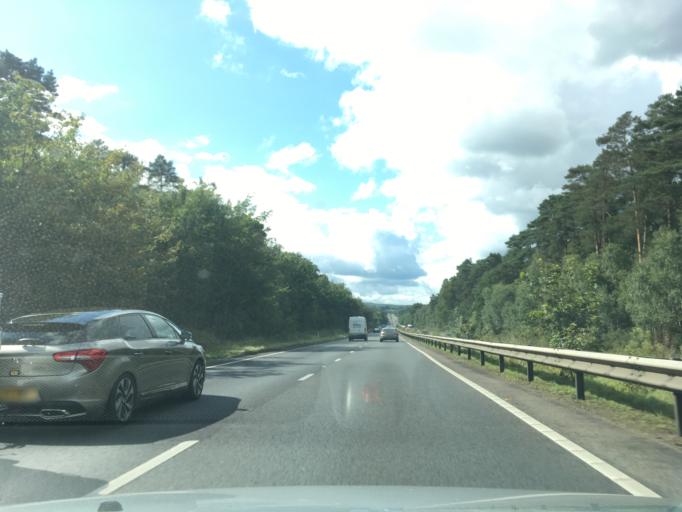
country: GB
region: England
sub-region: Surrey
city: Milford
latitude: 51.1595
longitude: -0.6763
